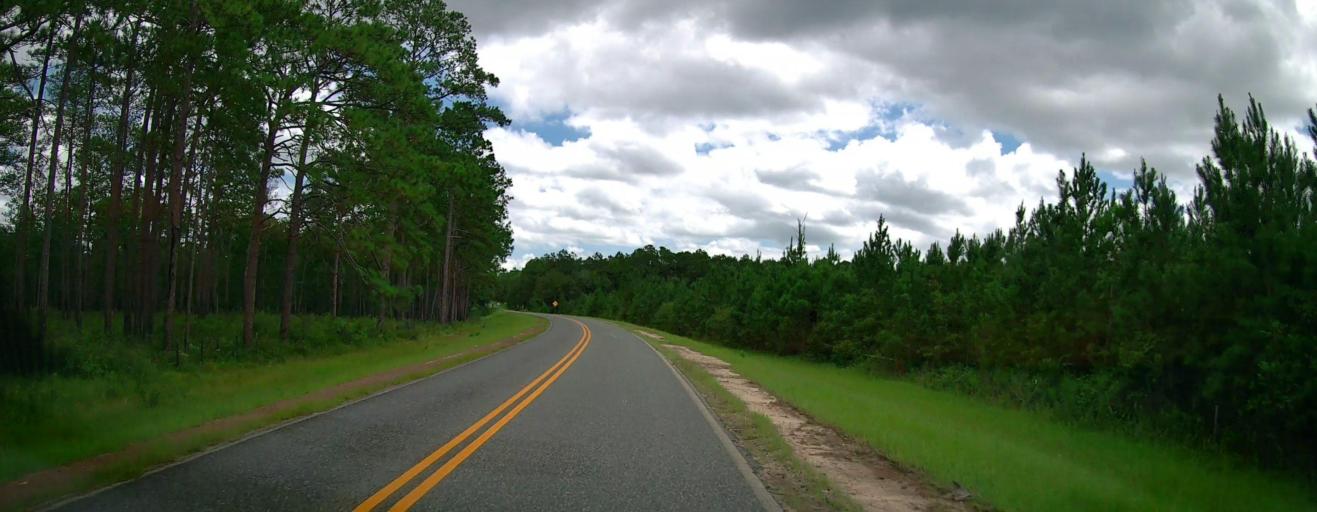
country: US
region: Georgia
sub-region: Turner County
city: Ashburn
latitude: 31.7046
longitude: -83.5046
